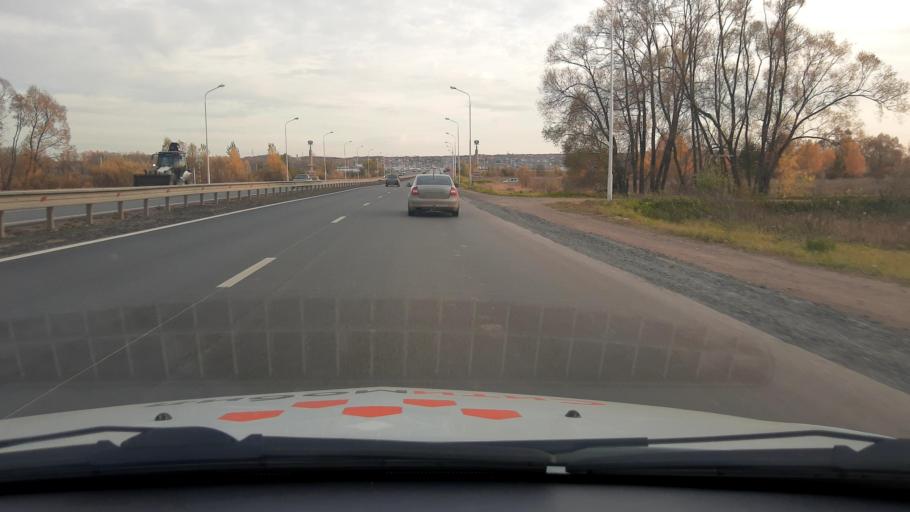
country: RU
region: Bashkortostan
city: Kabakovo
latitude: 54.6579
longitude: 56.0814
